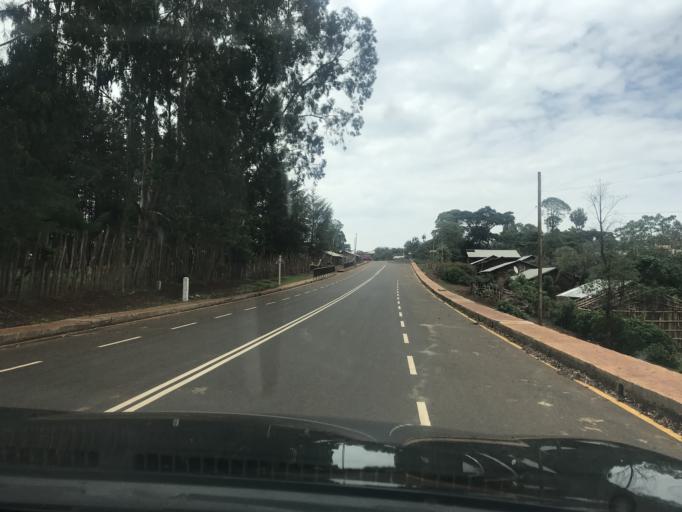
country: ET
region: Oromiya
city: Shambu
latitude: 9.8688
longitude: 36.6831
